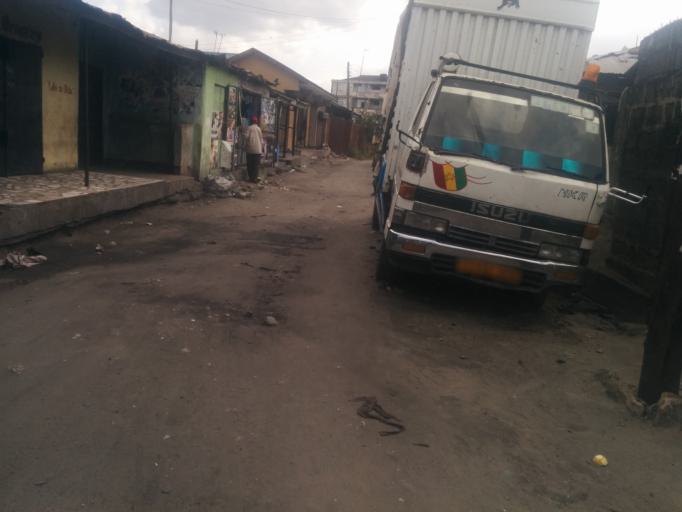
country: TZ
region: Dar es Salaam
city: Magomeni
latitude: -6.7983
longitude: 39.2369
